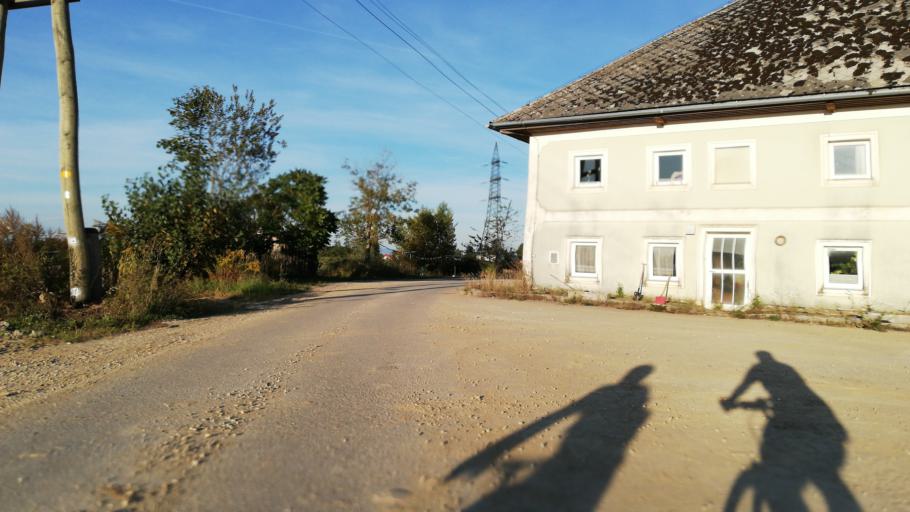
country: AT
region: Upper Austria
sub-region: Wels-Land
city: Offenhausen
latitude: 48.1651
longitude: 13.8591
